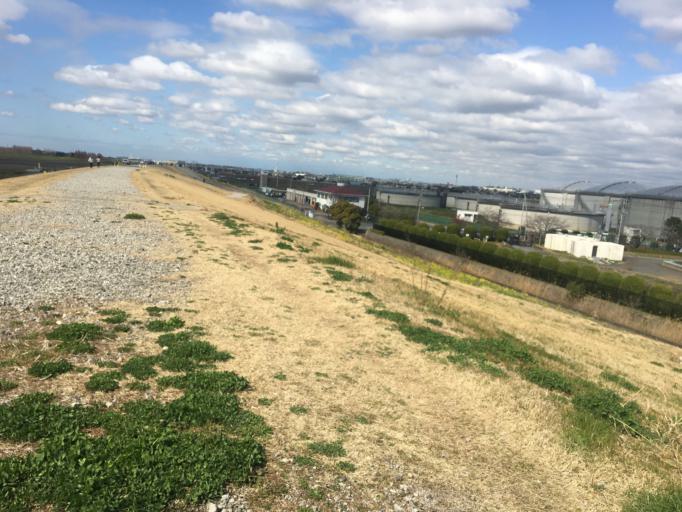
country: JP
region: Saitama
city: Shiki
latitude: 35.8761
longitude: 139.5847
